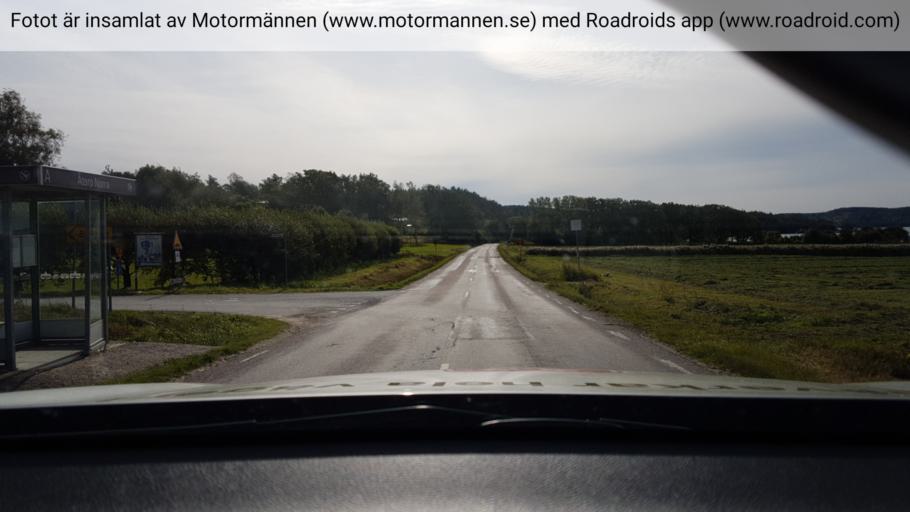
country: SE
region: Vaestra Goetaland
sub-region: Uddevalla Kommun
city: Ljungskile
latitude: 58.2773
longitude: 11.8496
